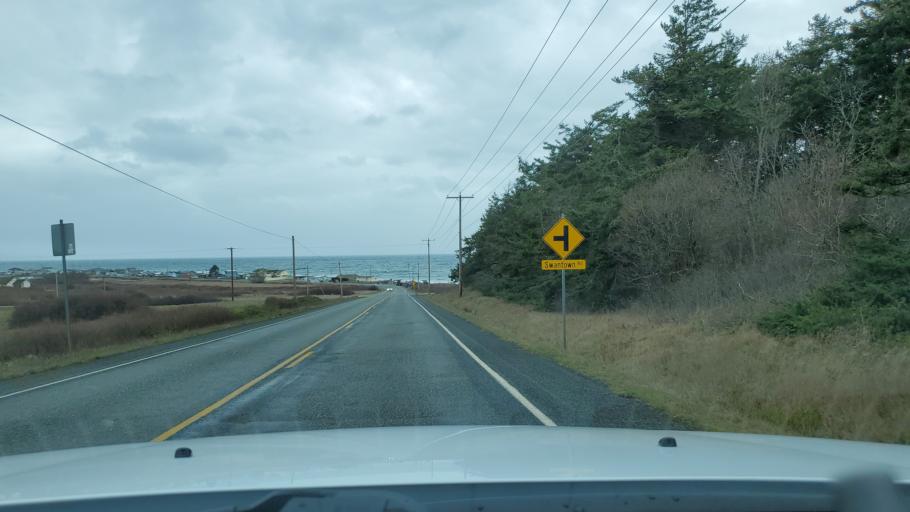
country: US
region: Washington
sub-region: Island County
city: Ault Field
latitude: 48.3082
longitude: -122.7083
